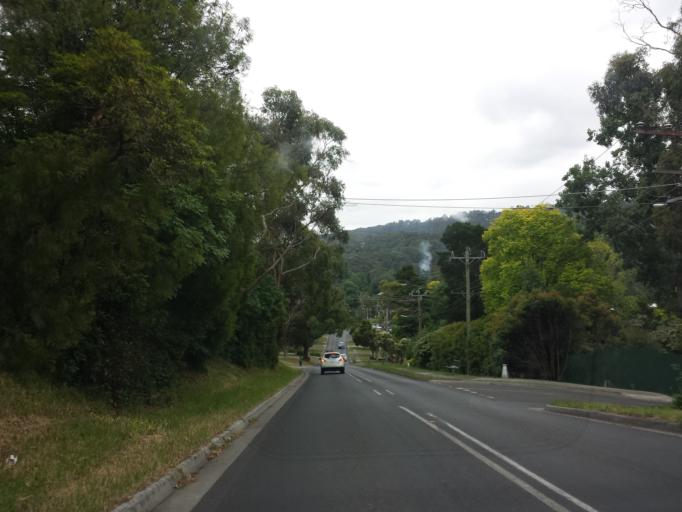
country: AU
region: Victoria
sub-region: Yarra Ranges
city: Tremont
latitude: -37.9057
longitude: 145.3296
